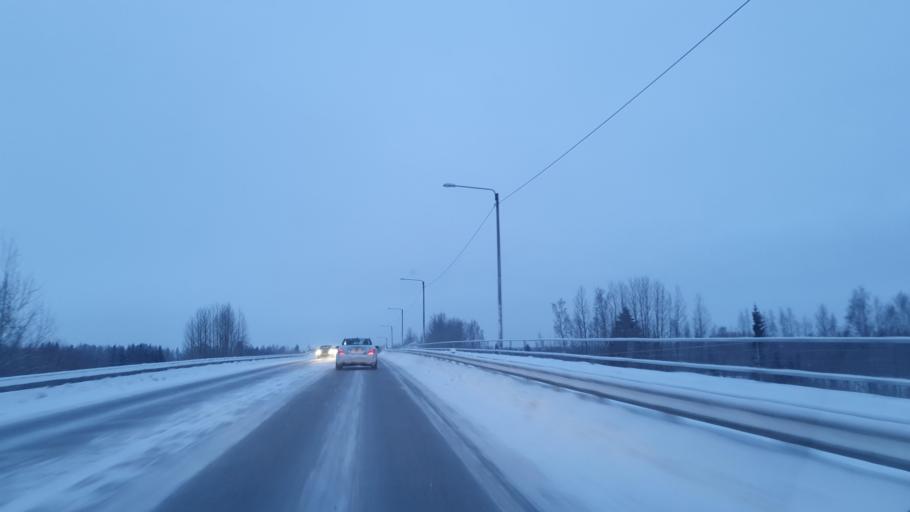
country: FI
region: Northern Ostrobothnia
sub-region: Oulu
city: Muhos
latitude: 64.8024
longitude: 26.0391
